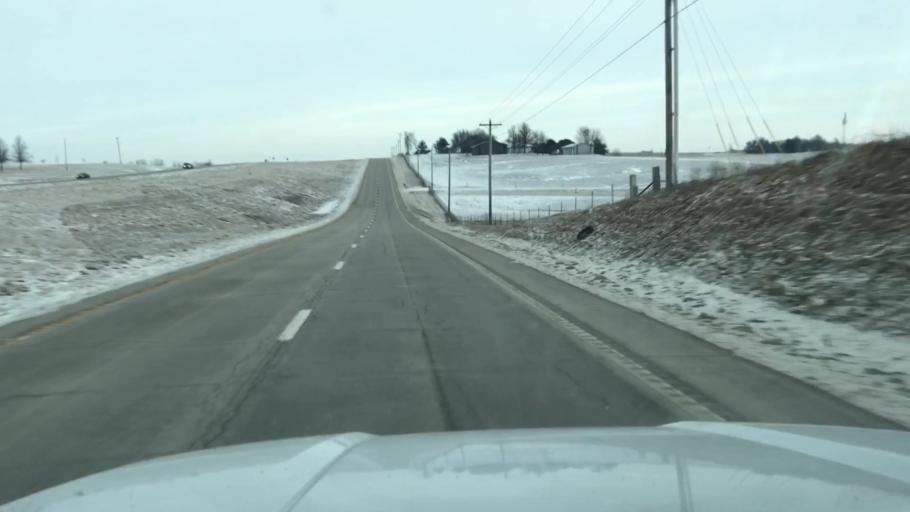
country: US
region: Missouri
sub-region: Andrew County
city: Savannah
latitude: 39.9885
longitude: -94.8798
